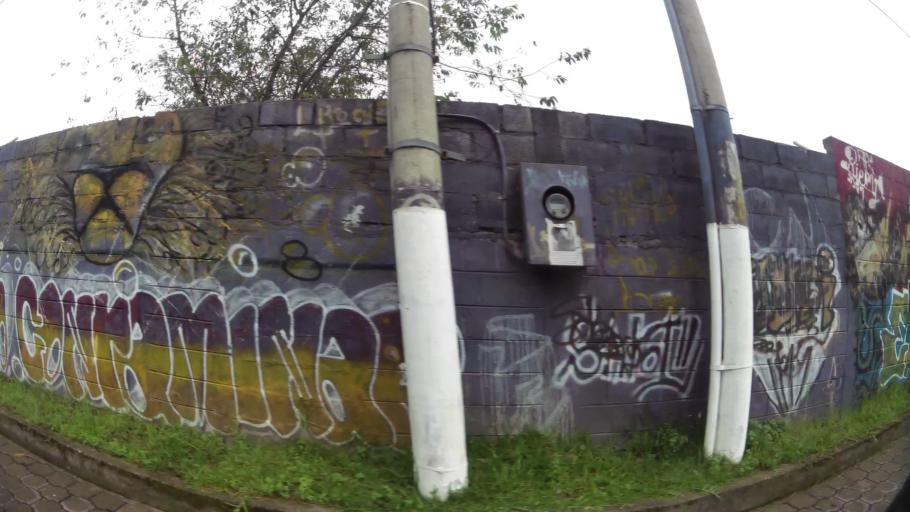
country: EC
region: Pichincha
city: Sangolqui
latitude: -0.2999
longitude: -78.4737
